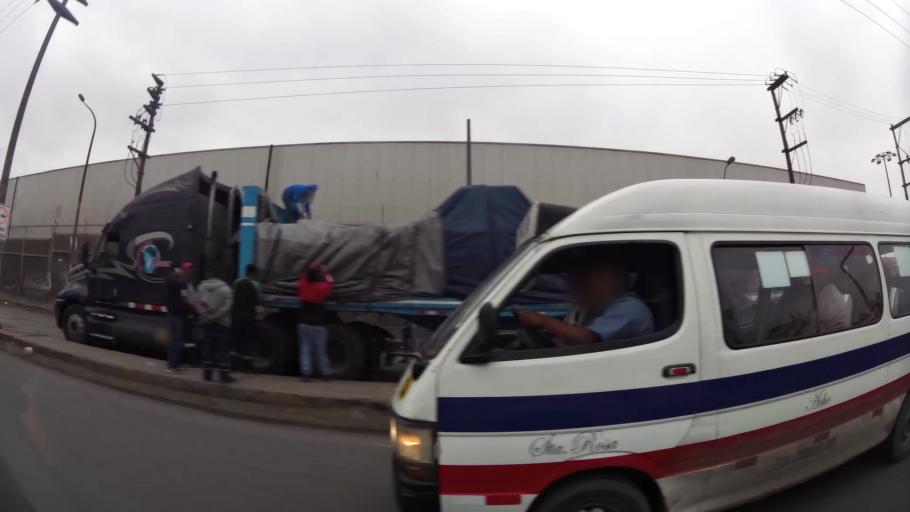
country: PE
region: Lima
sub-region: Lima
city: Vitarte
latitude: -12.0500
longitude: -76.9538
